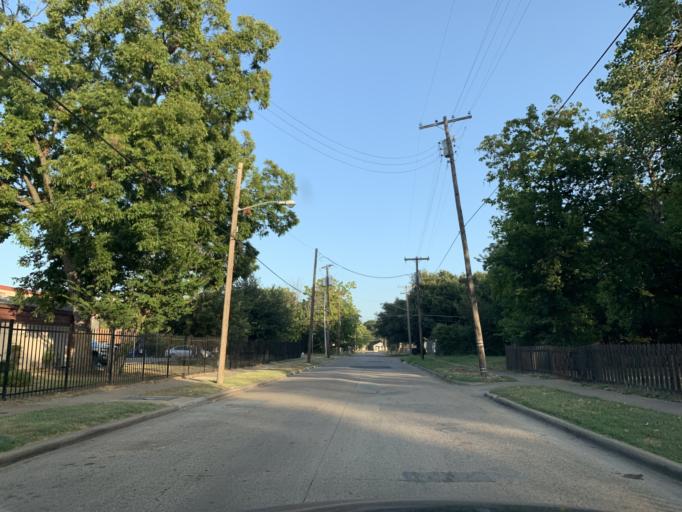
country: US
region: Texas
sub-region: Dallas County
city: Dallas
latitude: 32.7536
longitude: -96.7607
